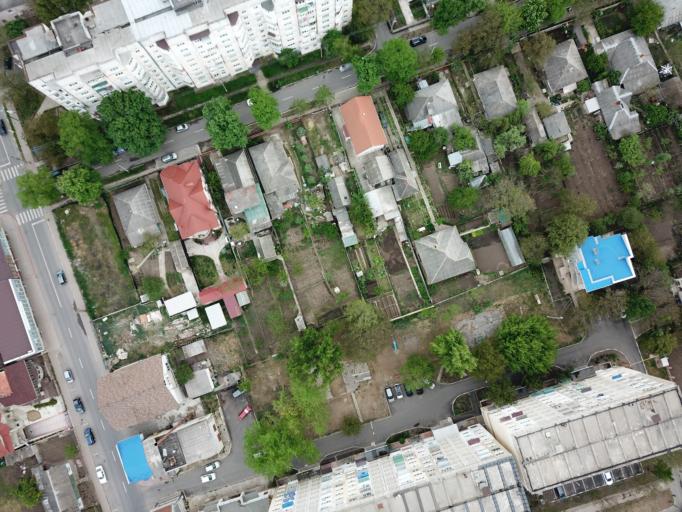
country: MD
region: Ungheni
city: Ungheni
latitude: 47.2083
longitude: 27.7971
